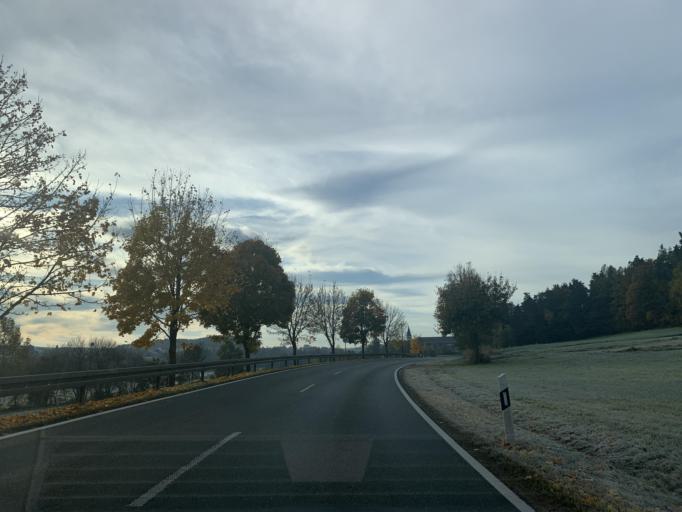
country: DE
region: Bavaria
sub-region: Upper Palatinate
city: Bach
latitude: 49.3763
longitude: 12.3763
